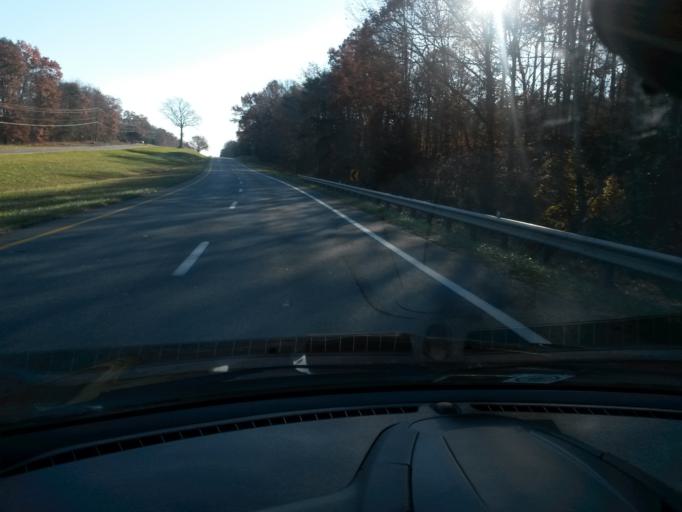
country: US
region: Virginia
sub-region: Appomattox County
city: Appomattox
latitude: 37.2880
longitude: -78.7281
